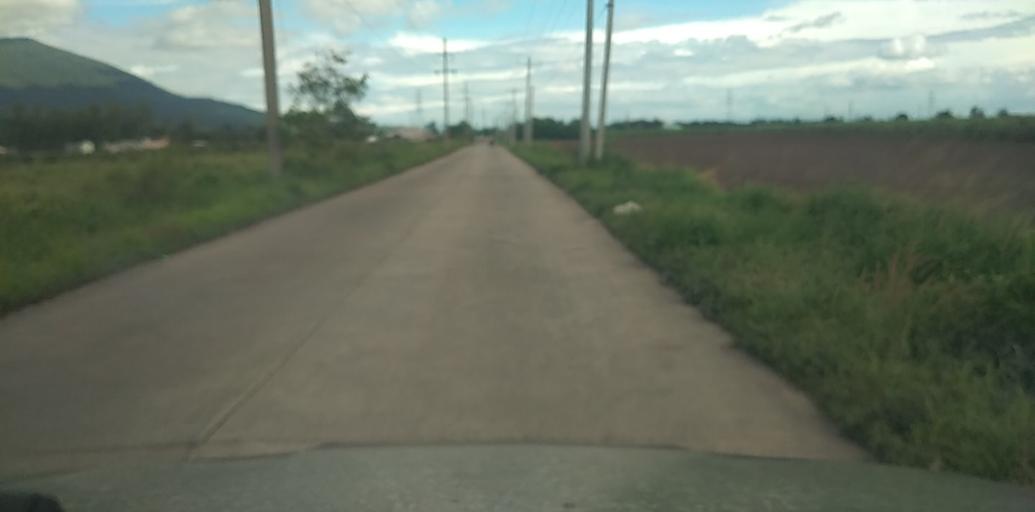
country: PH
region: Central Luzon
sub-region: Province of Pampanga
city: Arenas
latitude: 15.1746
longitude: 120.6709
